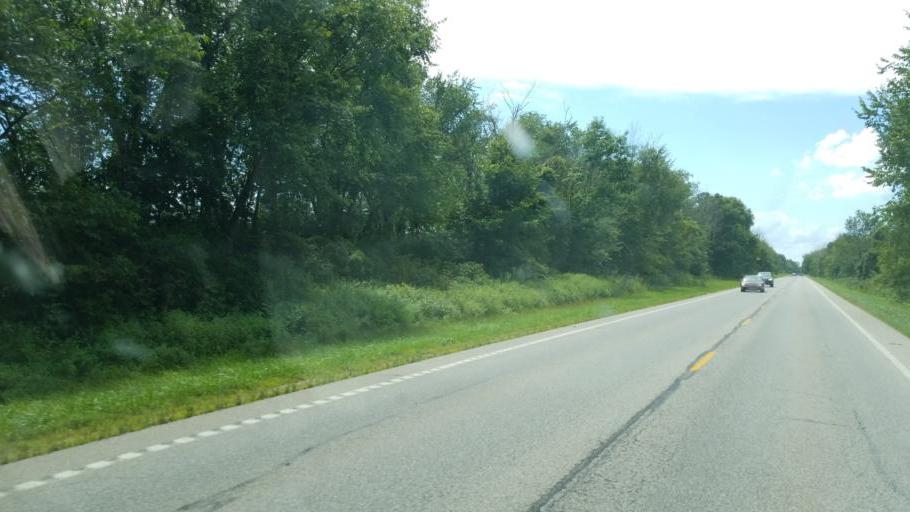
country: US
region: Ohio
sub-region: Delaware County
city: Sunbury
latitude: 40.2542
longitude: -82.8126
